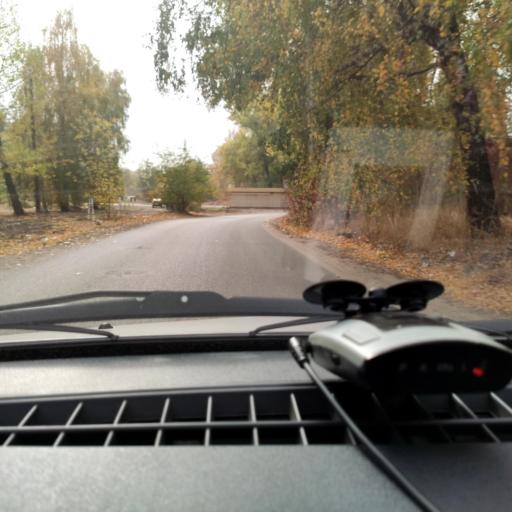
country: RU
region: Voronezj
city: Podgornoye
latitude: 51.7425
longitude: 39.1732
